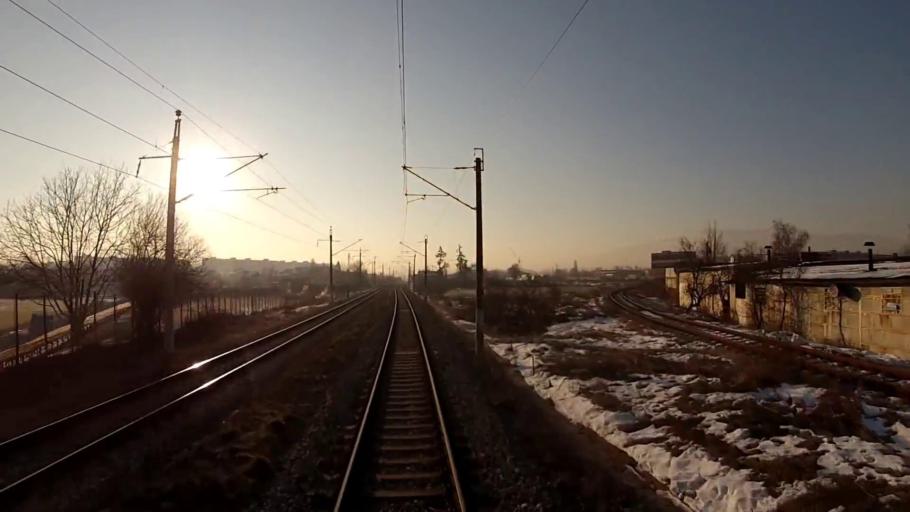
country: BG
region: Sofiya
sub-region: Obshtina Bozhurishte
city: Bozhurishte
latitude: 42.7481
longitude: 23.2527
